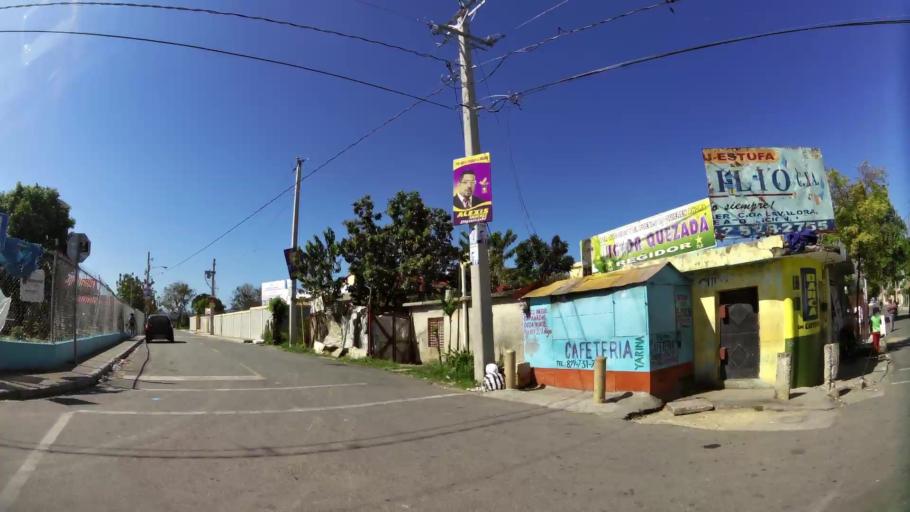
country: DO
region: San Cristobal
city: San Cristobal
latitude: 18.4257
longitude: -70.1329
